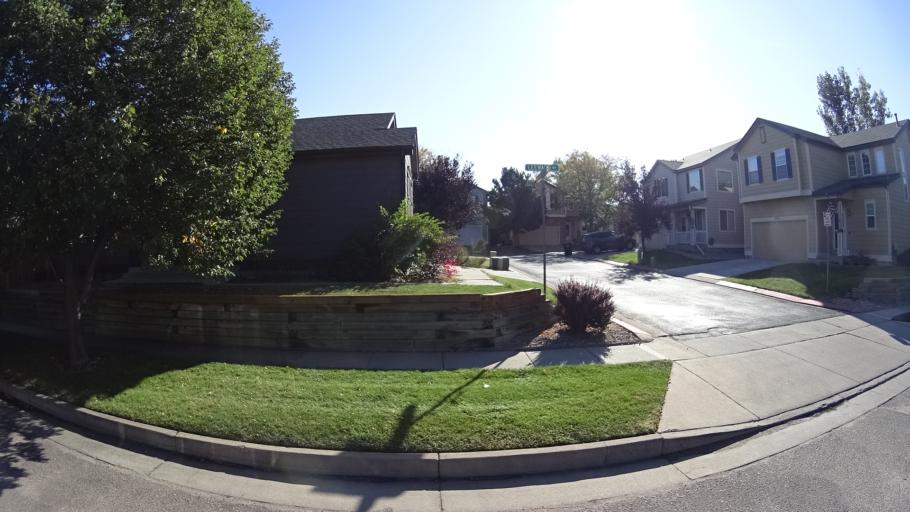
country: US
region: Colorado
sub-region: El Paso County
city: Cimarron Hills
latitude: 38.8786
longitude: -104.6958
